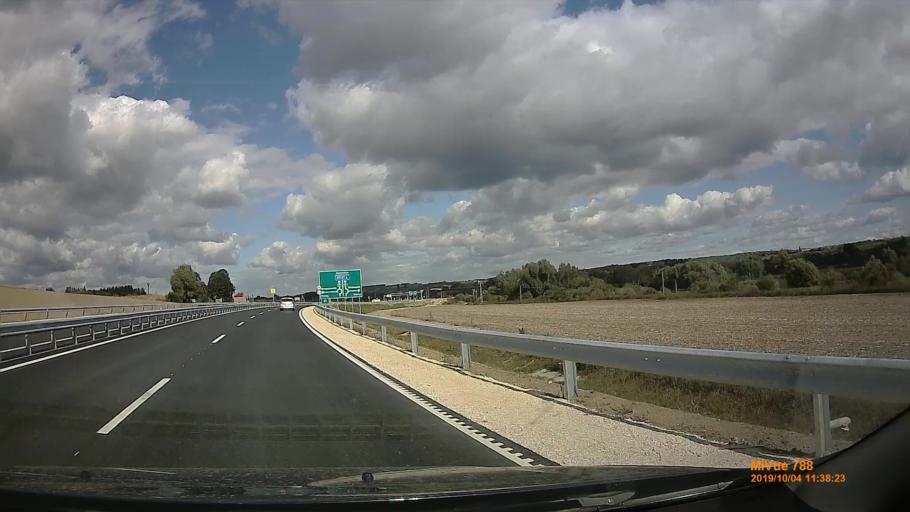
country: HU
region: Somogy
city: Karad
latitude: 46.5469
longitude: 17.8141
